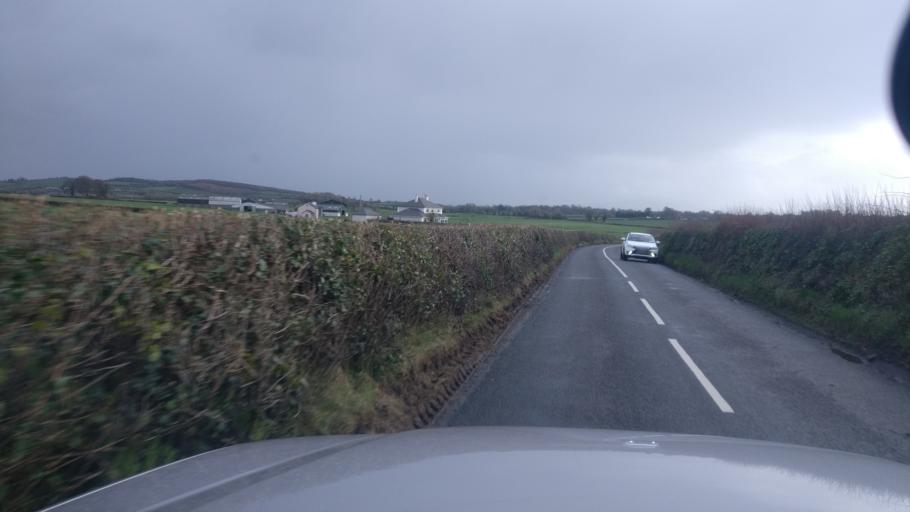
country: IE
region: Munster
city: Nenagh Bridge
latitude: 52.9654
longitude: -8.0864
